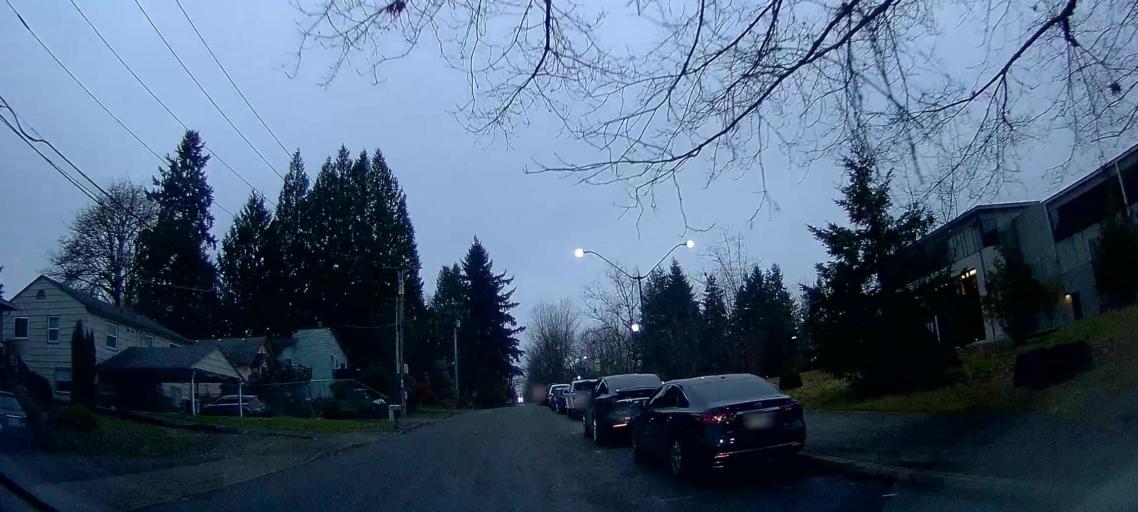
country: US
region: Washington
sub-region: Thurston County
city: Olympia
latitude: 47.0337
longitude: -122.8943
